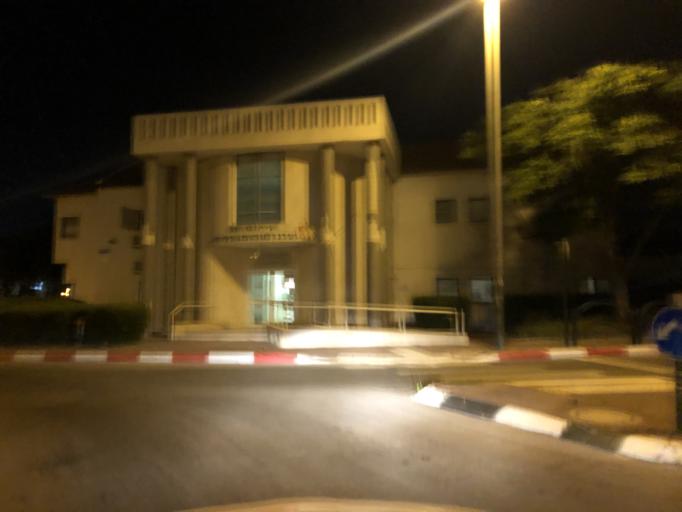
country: IL
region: Central District
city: Kfar Saba
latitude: 32.1816
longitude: 34.9354
